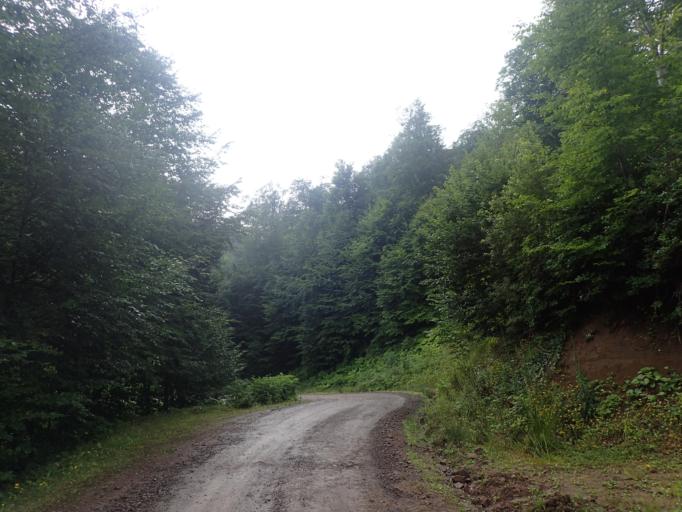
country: TR
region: Ordu
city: Akkus
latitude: 40.8117
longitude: 37.0968
